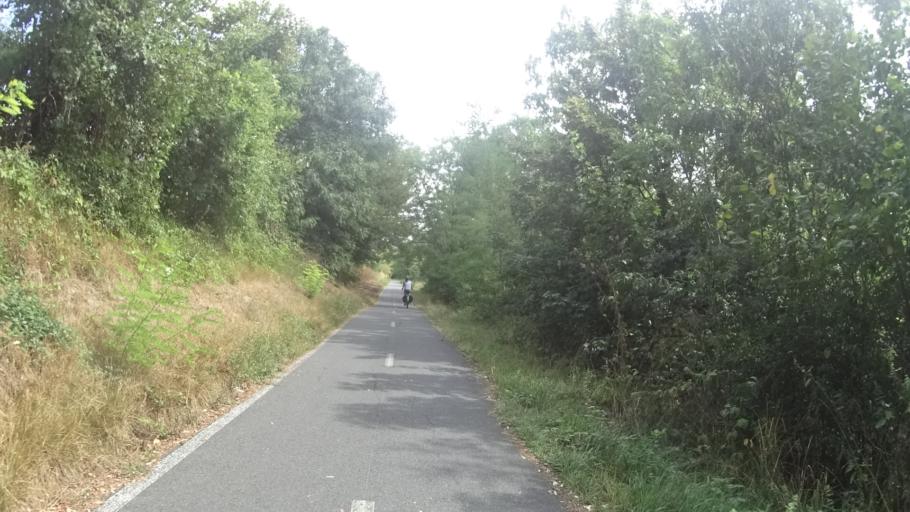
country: FR
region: Ile-de-France
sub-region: Departement de Seine-et-Marne
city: Villeparisis
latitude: 48.9518
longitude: 2.6075
